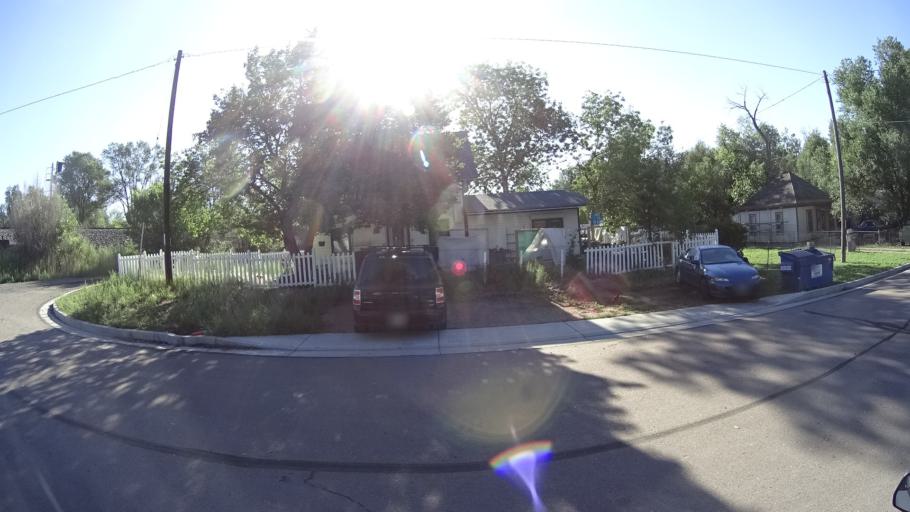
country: US
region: Colorado
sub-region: El Paso County
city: Colorado Springs
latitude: 38.8195
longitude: -104.8206
